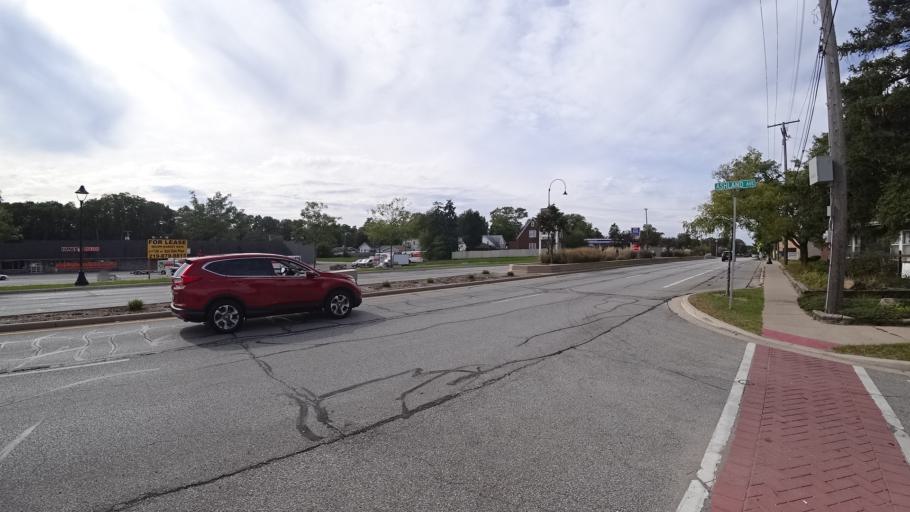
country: US
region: Indiana
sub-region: LaPorte County
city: Trail Creek
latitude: 41.7091
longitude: -86.8707
